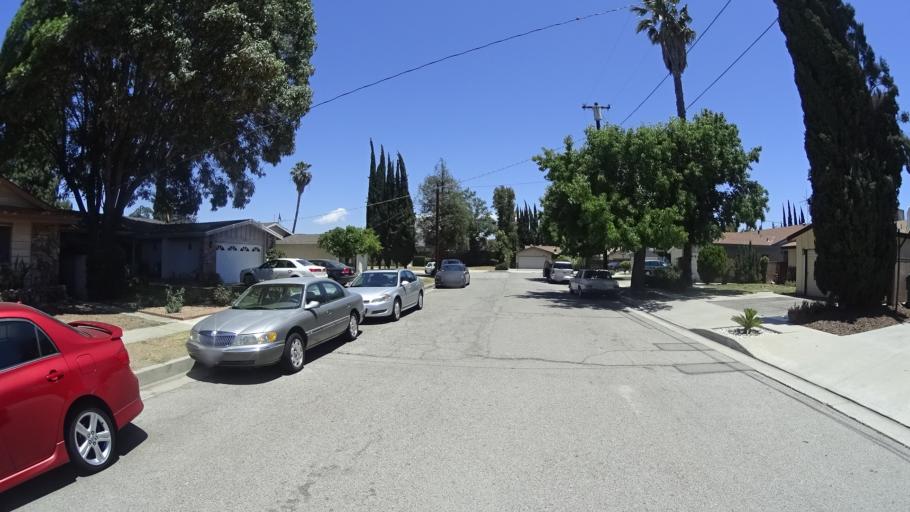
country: US
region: California
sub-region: Los Angeles County
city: Van Nuys
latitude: 34.2057
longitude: -118.4688
